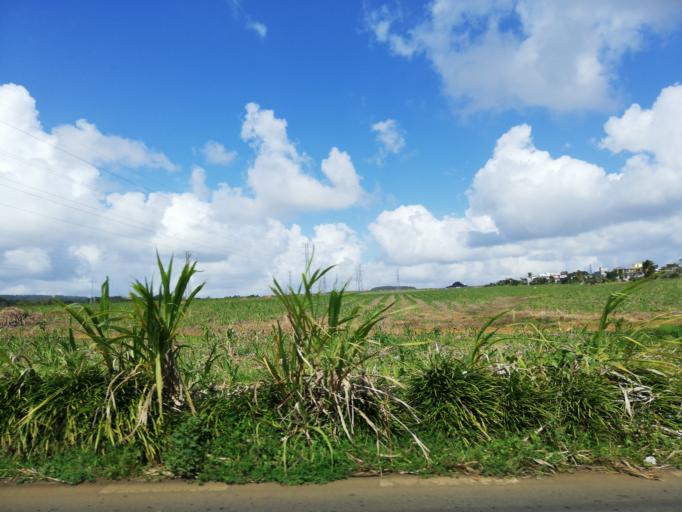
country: MU
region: Moka
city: Verdun
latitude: -20.2148
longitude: 57.5532
